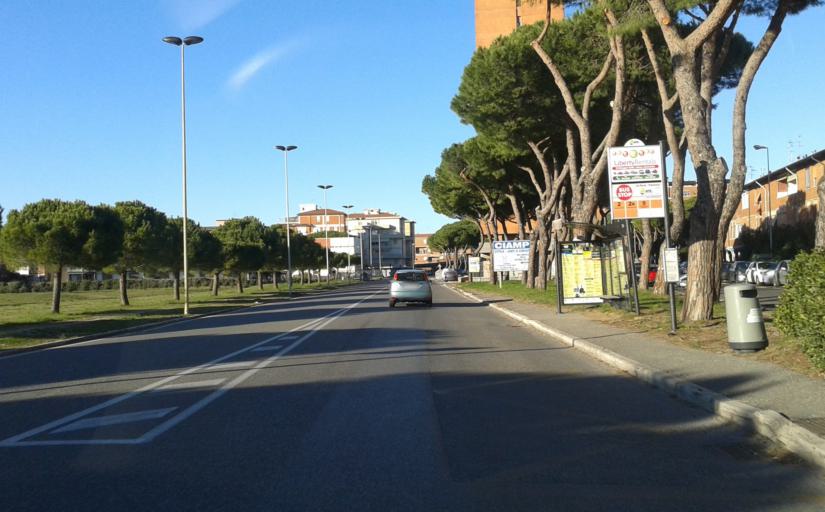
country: IT
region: Tuscany
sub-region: Provincia di Livorno
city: Livorno
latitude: 43.5216
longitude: 10.3240
